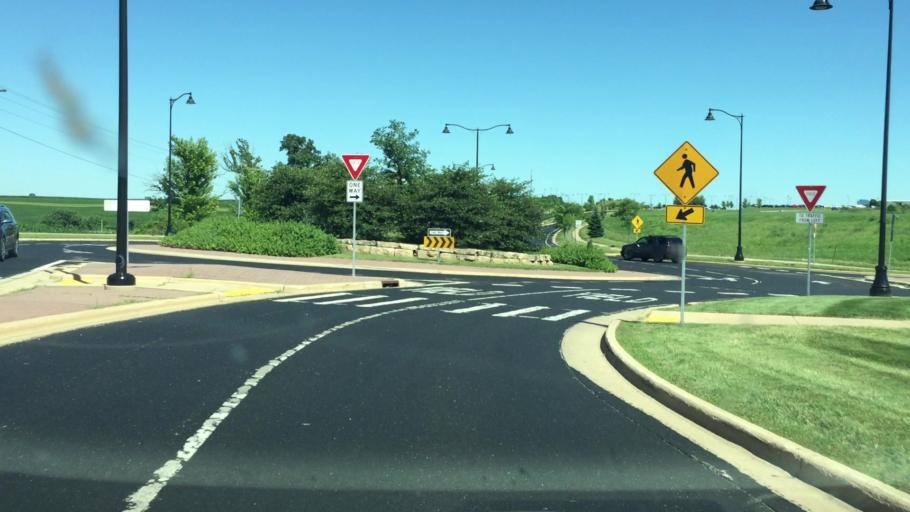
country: US
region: Wisconsin
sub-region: Dane County
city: Mount Horeb
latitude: 43.0092
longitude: -89.7111
